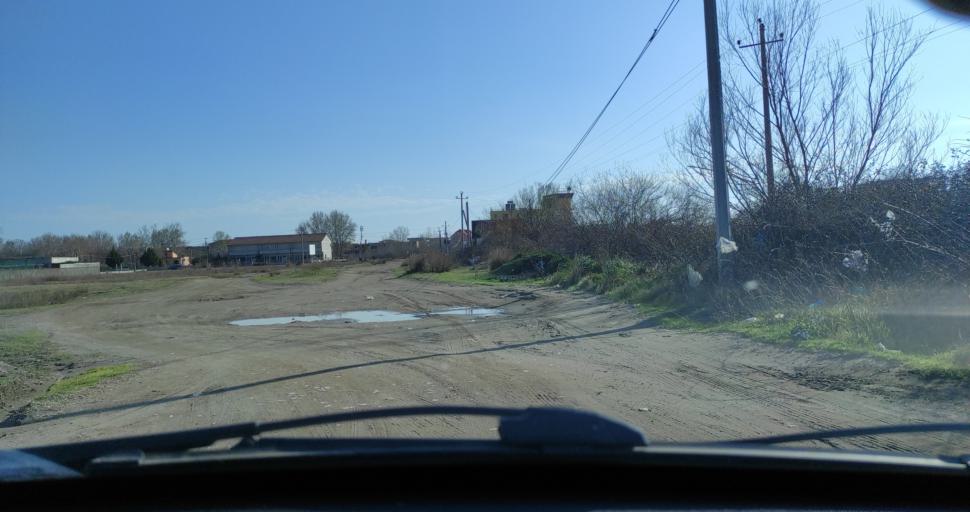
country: AL
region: Shkoder
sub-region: Rrethi i Shkodres
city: Velipoje
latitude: 41.8690
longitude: 19.4116
